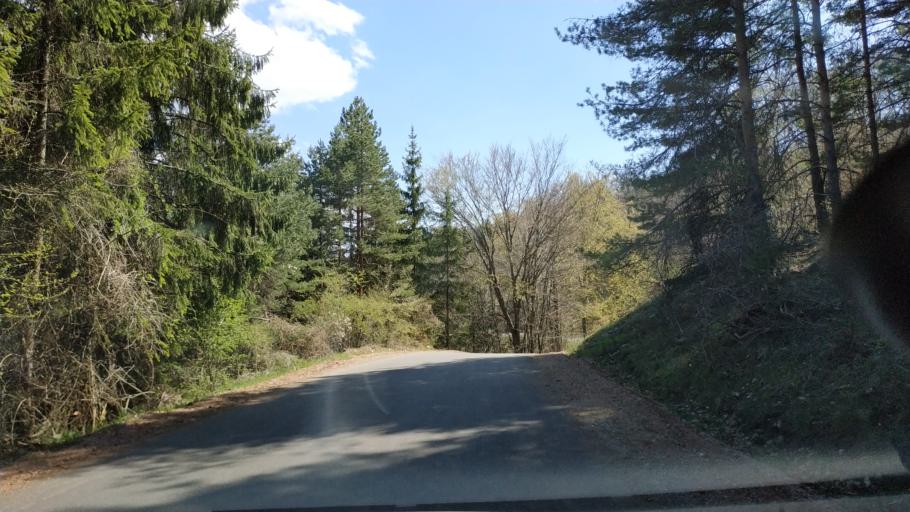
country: RS
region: Central Serbia
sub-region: Zajecarski Okrug
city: Soko Banja
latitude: 43.5880
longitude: 21.8872
